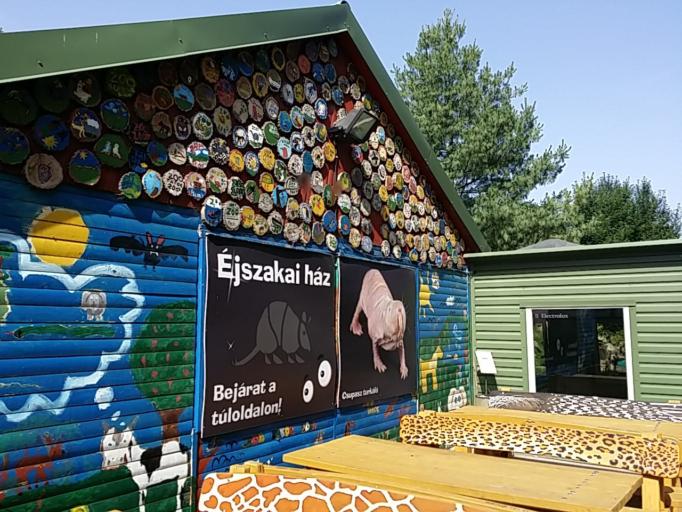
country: HU
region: Jasz-Nagykun-Szolnok
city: Jaszbereny
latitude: 47.4938
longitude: 19.8685
